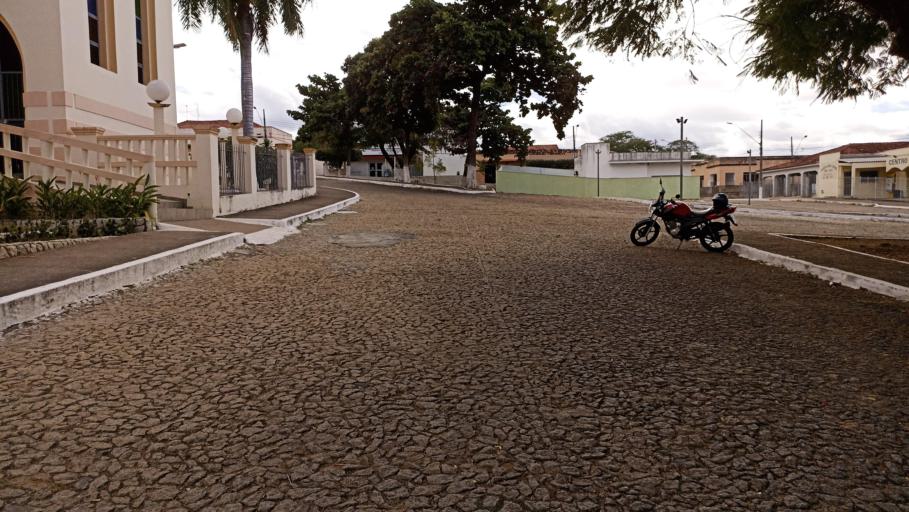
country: BR
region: Minas Gerais
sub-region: Joaima
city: Joaima
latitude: -16.6555
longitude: -41.0228
